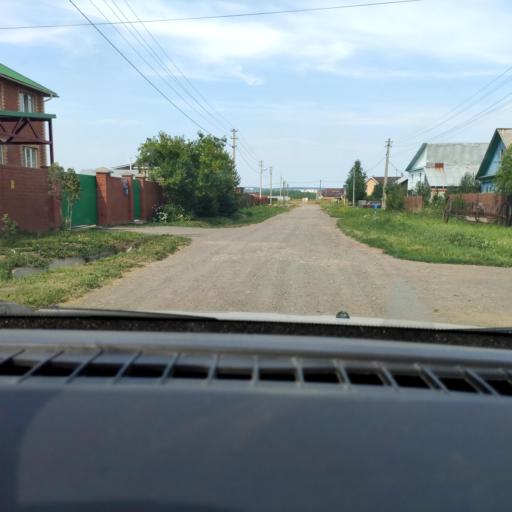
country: RU
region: Perm
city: Froly
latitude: 57.8906
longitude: 56.2529
